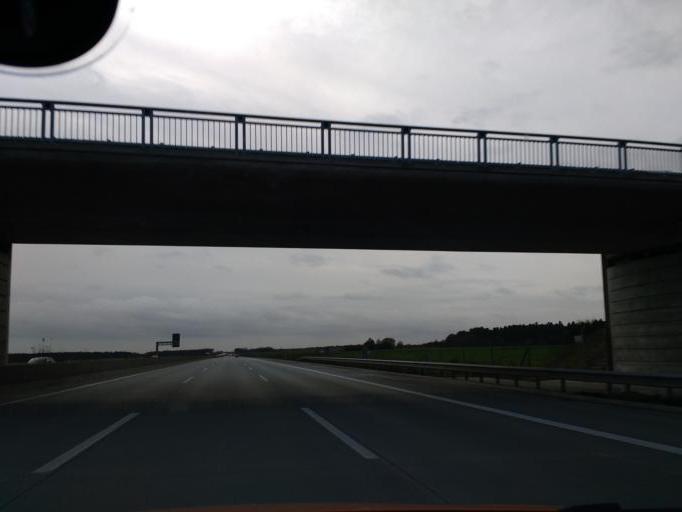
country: DE
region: Lower Saxony
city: Gross Meckelsen
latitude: 53.2767
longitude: 9.4649
